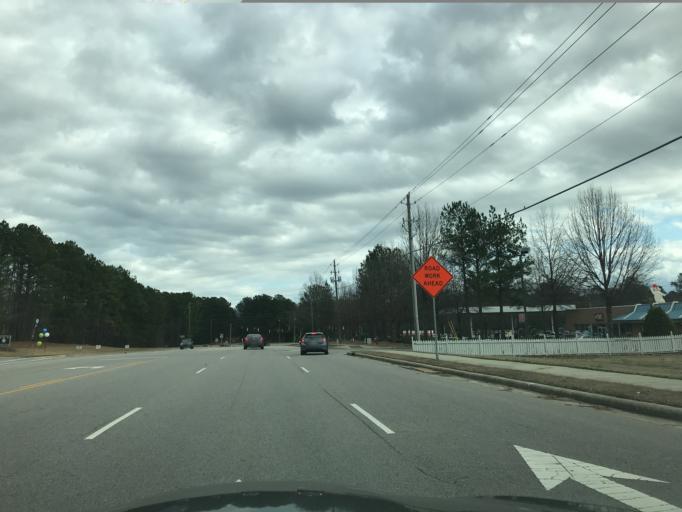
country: US
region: North Carolina
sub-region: Wake County
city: Knightdale
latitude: 35.8560
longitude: -78.5576
